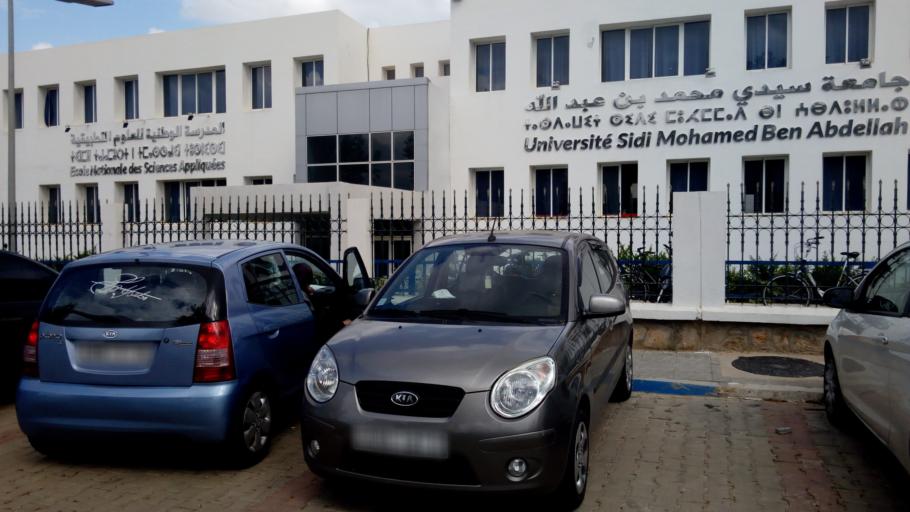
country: MA
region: Fes-Boulemane
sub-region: Fes
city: Fes
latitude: 33.9967
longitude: -4.9920
